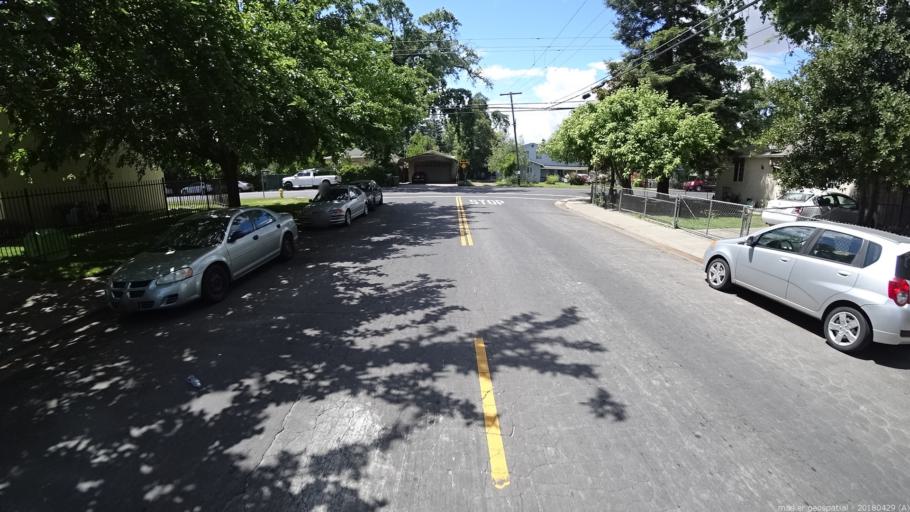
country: US
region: California
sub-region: Yolo County
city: West Sacramento
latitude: 38.5942
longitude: -121.5379
